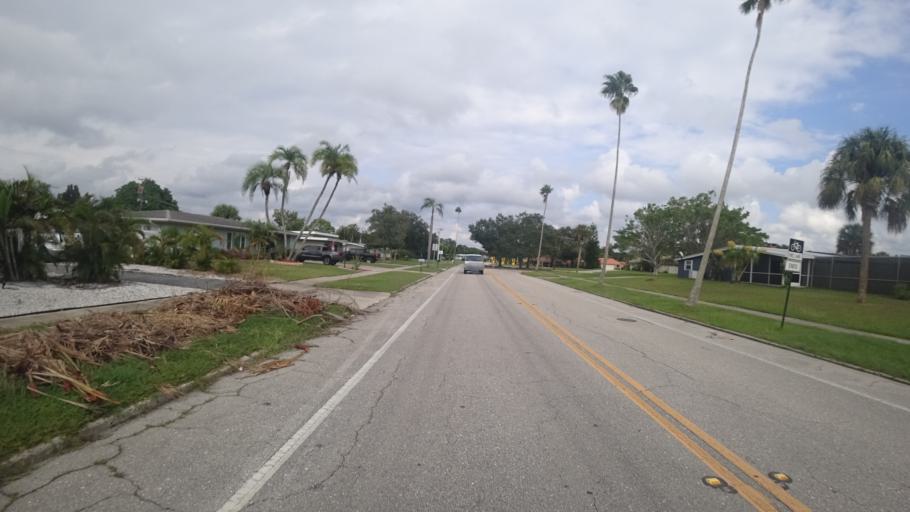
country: US
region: Florida
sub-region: Manatee County
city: Whitfield
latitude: 27.4132
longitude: -82.5683
